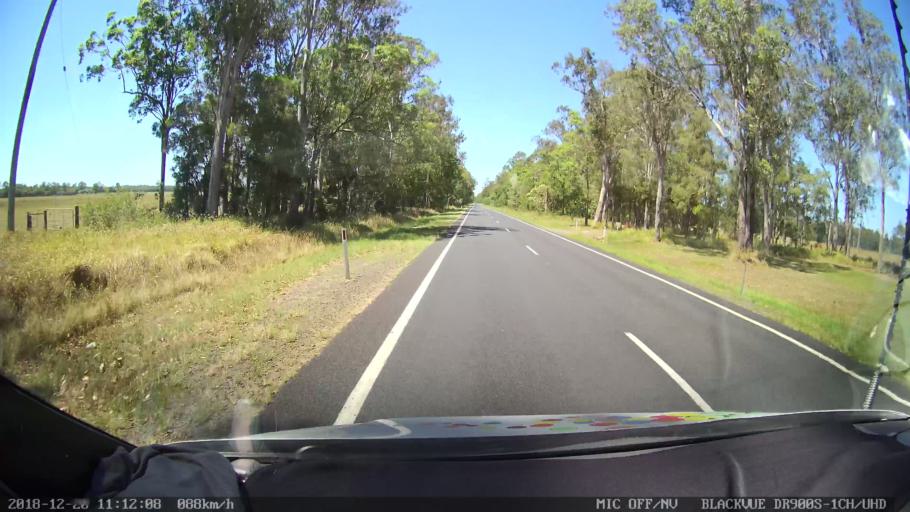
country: AU
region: New South Wales
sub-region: Richmond Valley
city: Casino
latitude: -28.9700
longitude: 153.0118
